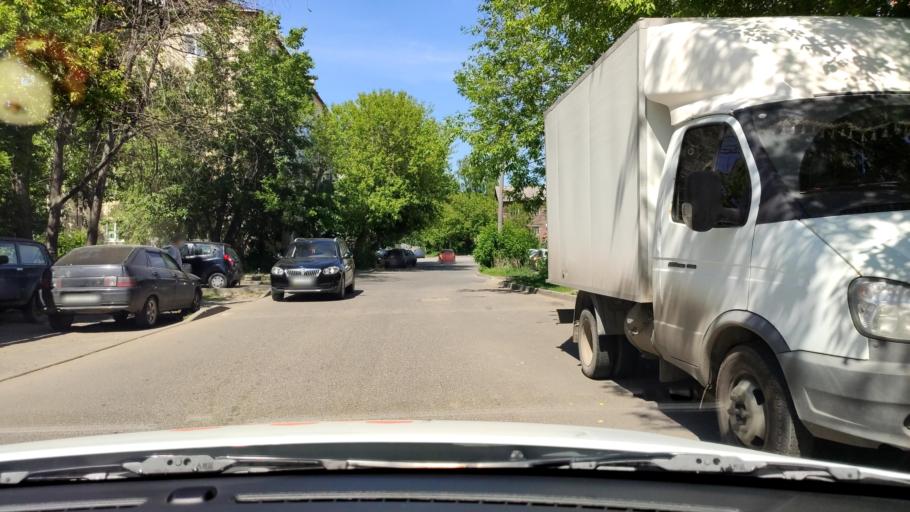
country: RU
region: Tatarstan
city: Osinovo
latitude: 55.8190
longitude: 48.8865
